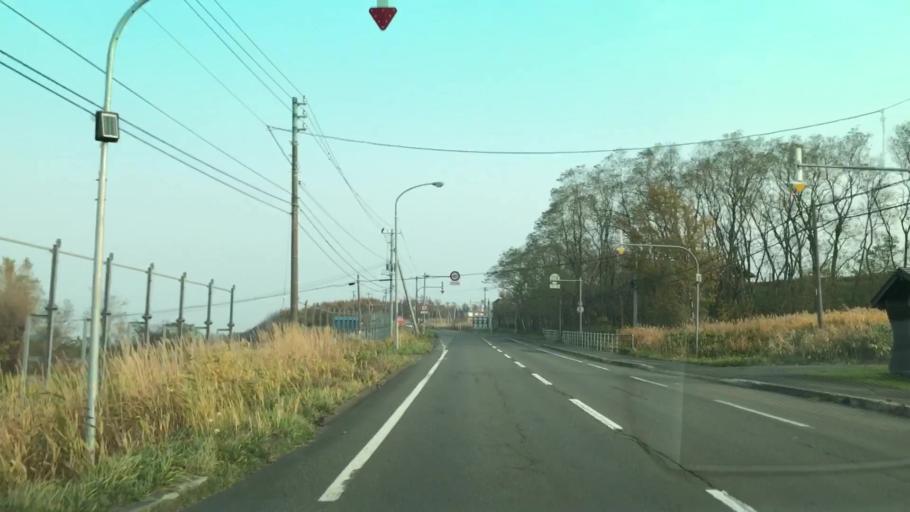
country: JP
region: Hokkaido
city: Ishikari
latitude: 43.2739
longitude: 141.4030
